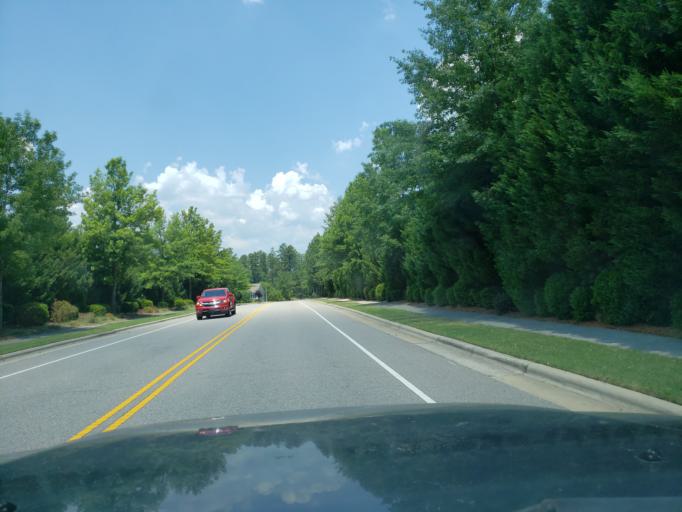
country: US
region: North Carolina
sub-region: Wake County
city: Green Level
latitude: 35.8321
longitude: -78.9141
